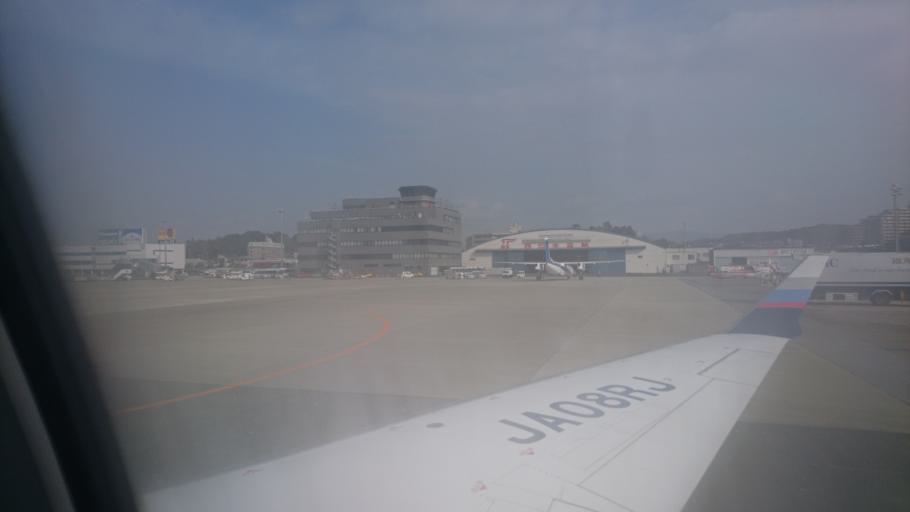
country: JP
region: Fukuoka
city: Fukuoka-shi
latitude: 33.5923
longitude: 130.4486
